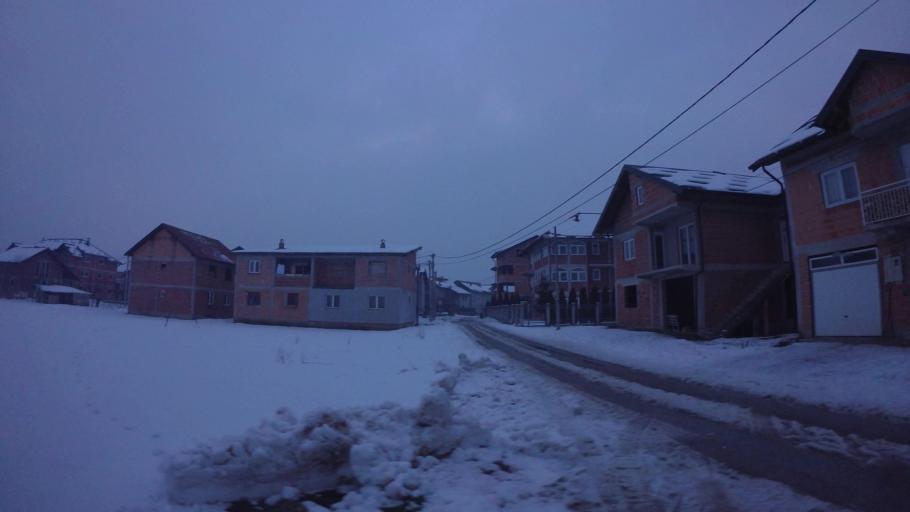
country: BA
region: Federation of Bosnia and Herzegovina
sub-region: Kanton Sarajevo
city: Sarajevo
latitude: 43.8512
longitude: 18.2906
